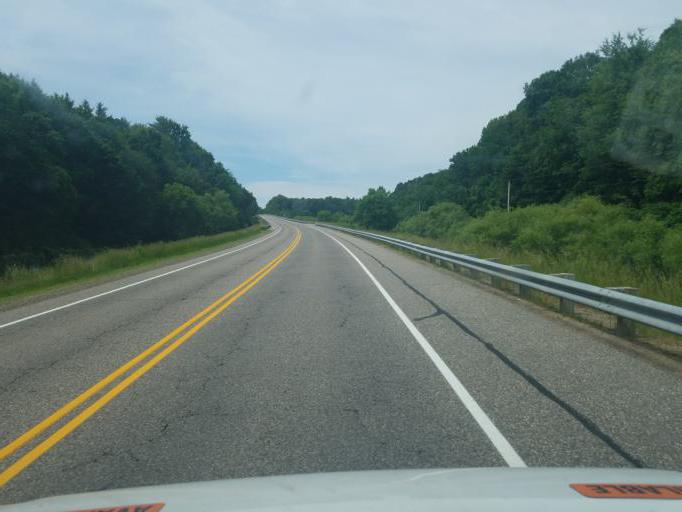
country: US
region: Wisconsin
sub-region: Juneau County
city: New Lisbon
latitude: 43.7876
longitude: -90.1858
